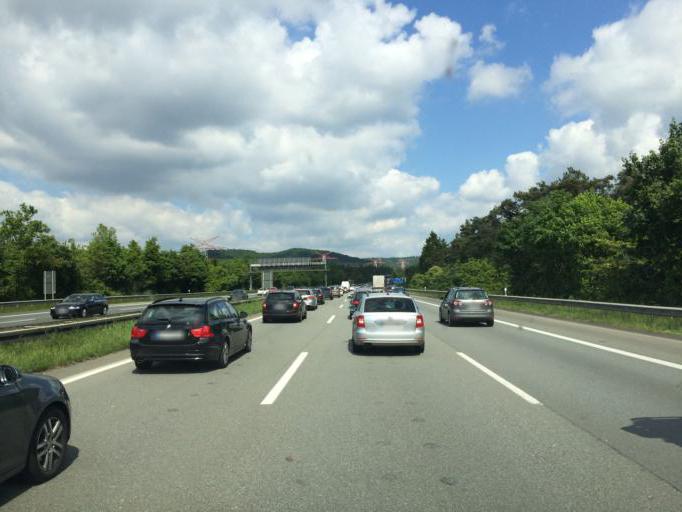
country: DE
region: North Rhine-Westphalia
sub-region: Regierungsbezirk Detmold
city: Bielefeld
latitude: 51.9563
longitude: 8.5732
